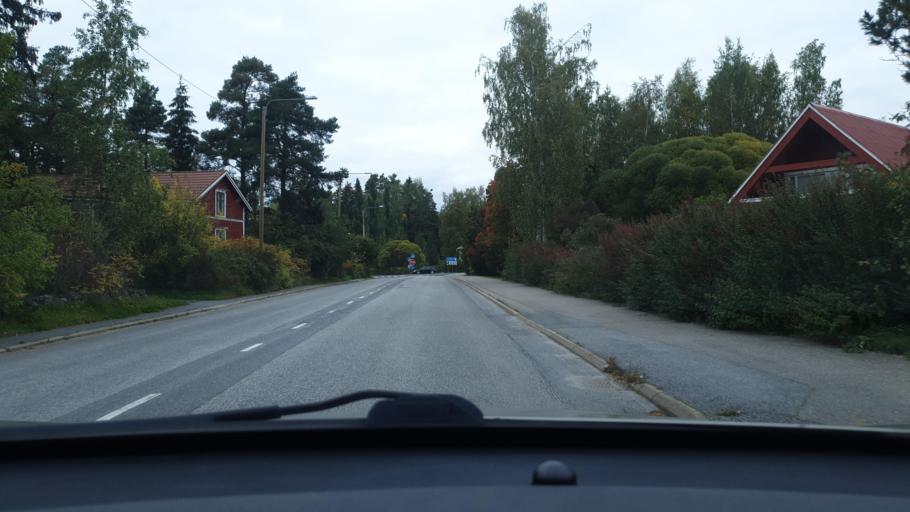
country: FI
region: Ostrobothnia
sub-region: Vaasa
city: Korsholm
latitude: 63.0984
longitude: 21.6686
